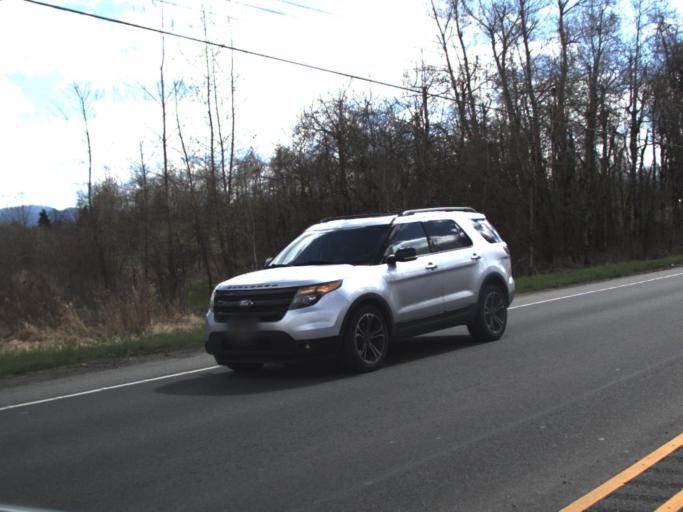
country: US
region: Washington
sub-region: King County
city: Lake Morton-Berrydale
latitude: 47.2531
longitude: -122.1204
